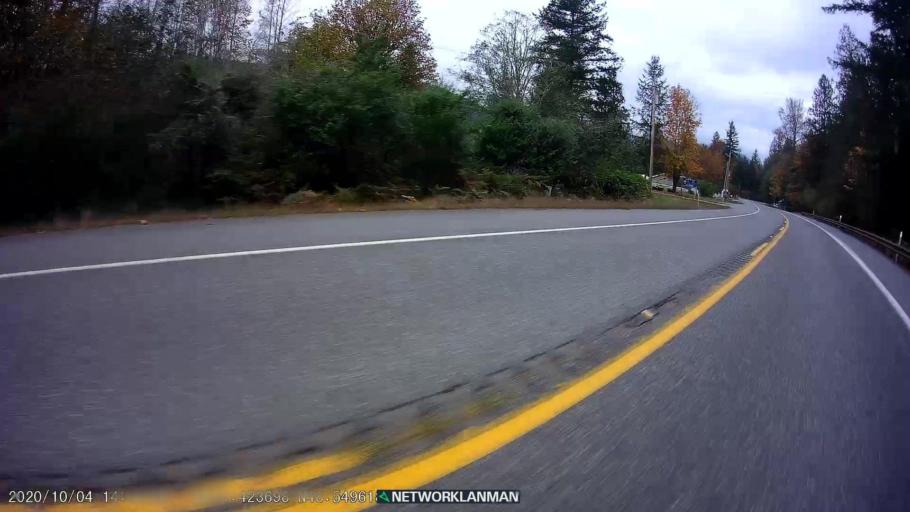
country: US
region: Washington
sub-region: Snohomish County
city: Darrington
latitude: 48.5501
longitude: -121.4235
